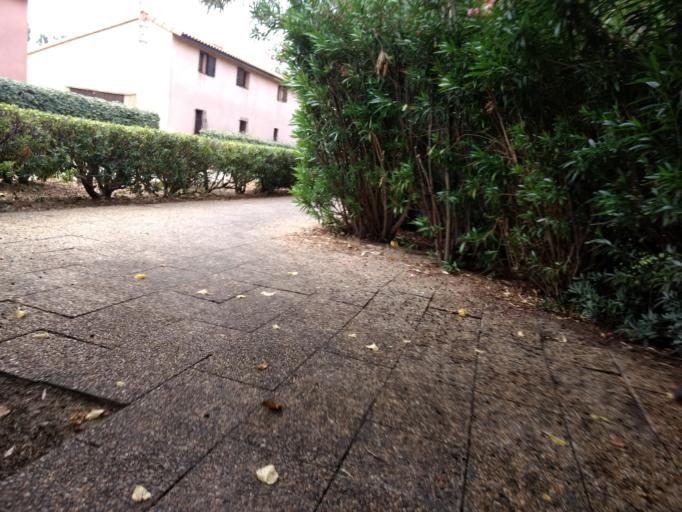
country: FR
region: Languedoc-Roussillon
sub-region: Departement de l'Aude
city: Leucate
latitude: 42.8568
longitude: 3.0402
